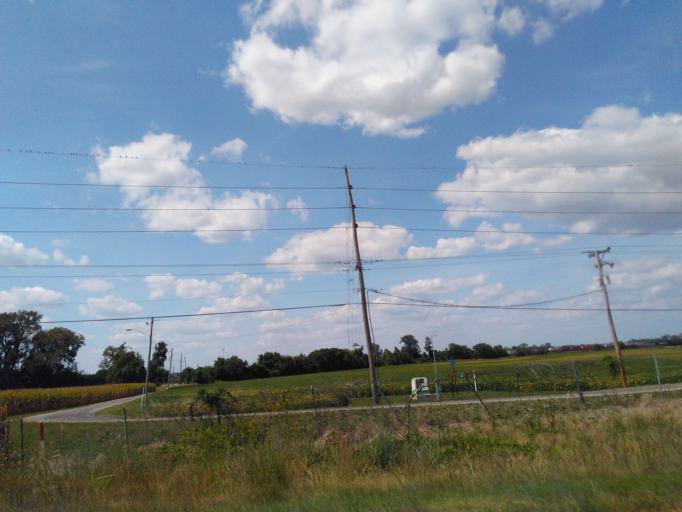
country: US
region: Illinois
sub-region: Saint Clair County
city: Dupo
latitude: 38.4965
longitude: -90.2142
